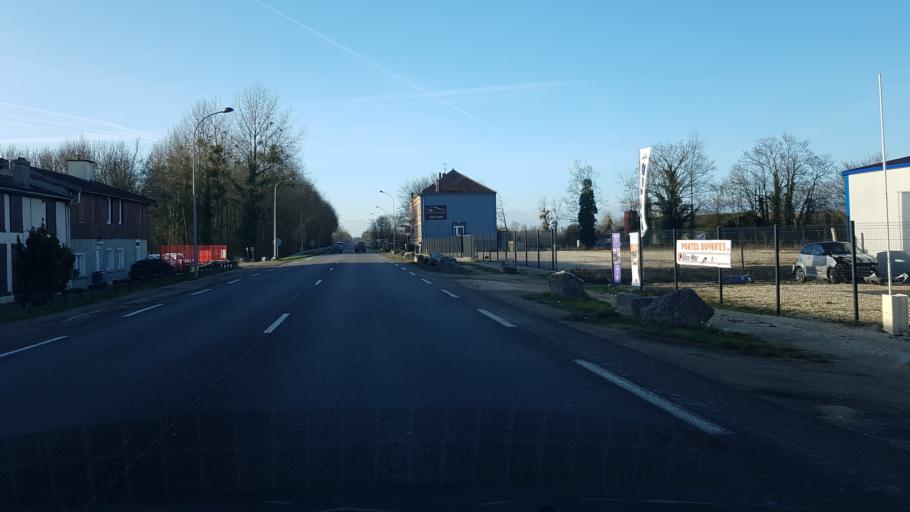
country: FR
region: Champagne-Ardenne
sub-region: Departement de la Marne
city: Vitry-le-Francois
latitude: 48.7291
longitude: 4.5745
